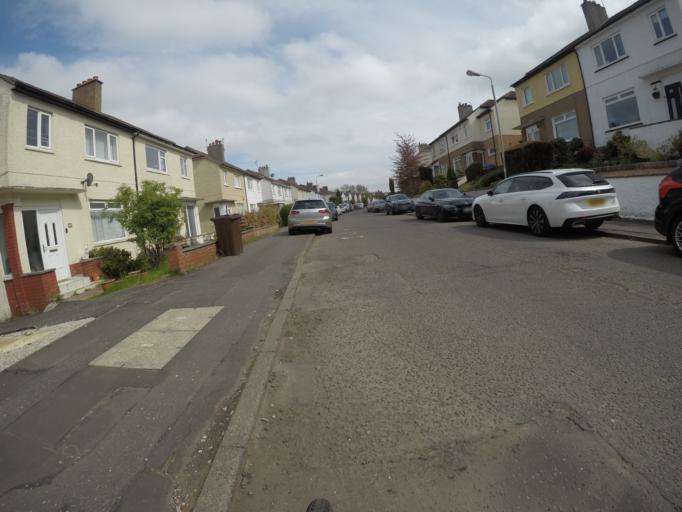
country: GB
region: Scotland
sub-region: East Renfrewshire
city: Giffnock
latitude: 55.8071
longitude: -4.2813
